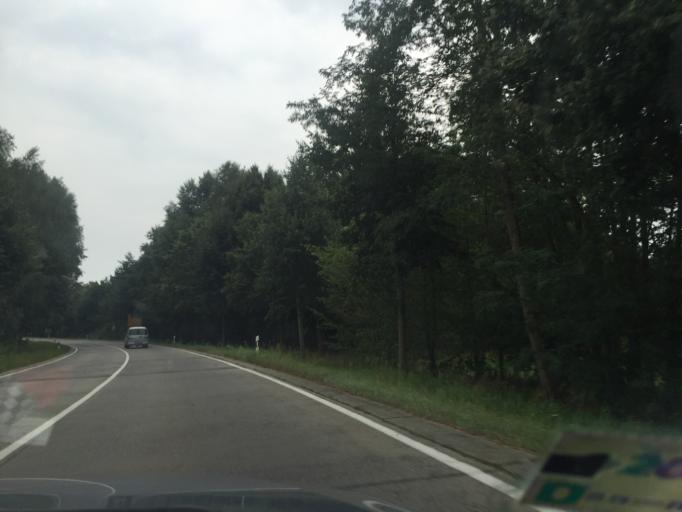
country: DE
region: Brandenburg
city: Wandlitz
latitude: 52.7484
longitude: 13.4289
